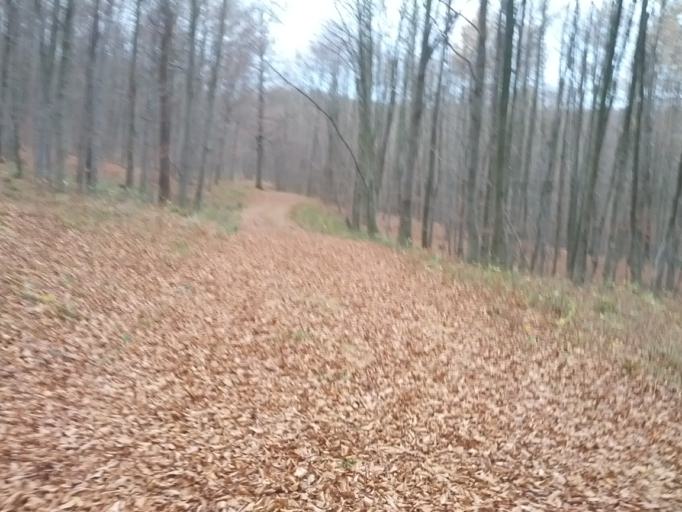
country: DE
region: Thuringia
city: Eisenach
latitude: 50.9354
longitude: 10.3191
